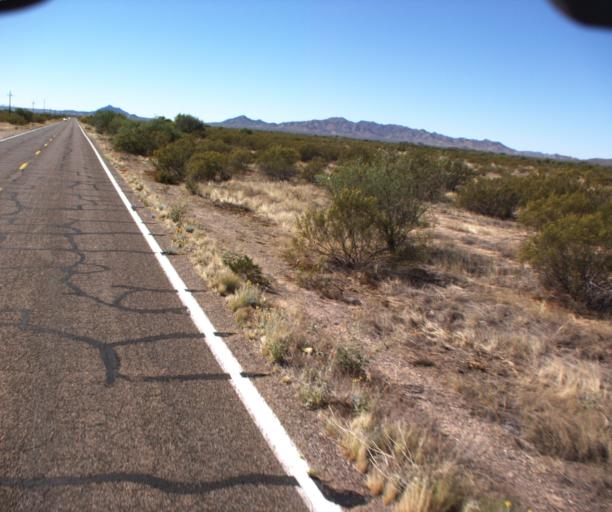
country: US
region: Arizona
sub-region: Pima County
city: Ajo
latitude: 32.4715
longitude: -112.8763
